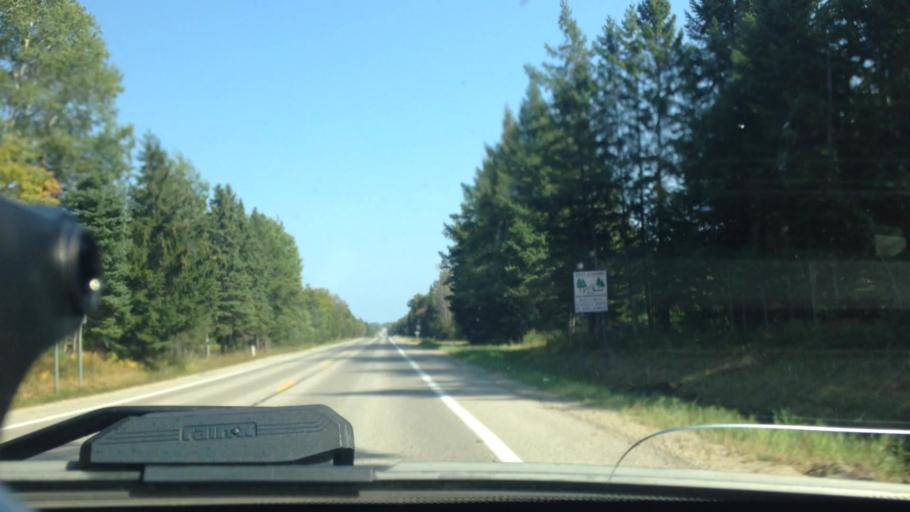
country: US
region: Michigan
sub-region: Luce County
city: Newberry
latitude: 46.3036
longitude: -85.4214
